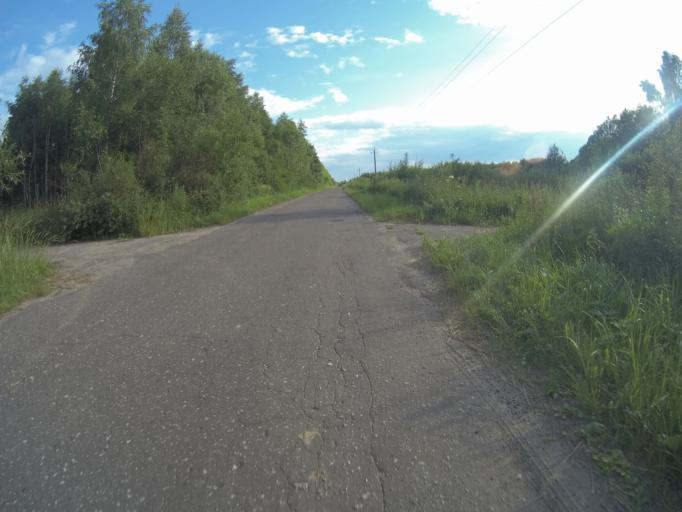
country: RU
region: Vladimir
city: Sudogda
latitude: 56.0482
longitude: 40.8861
